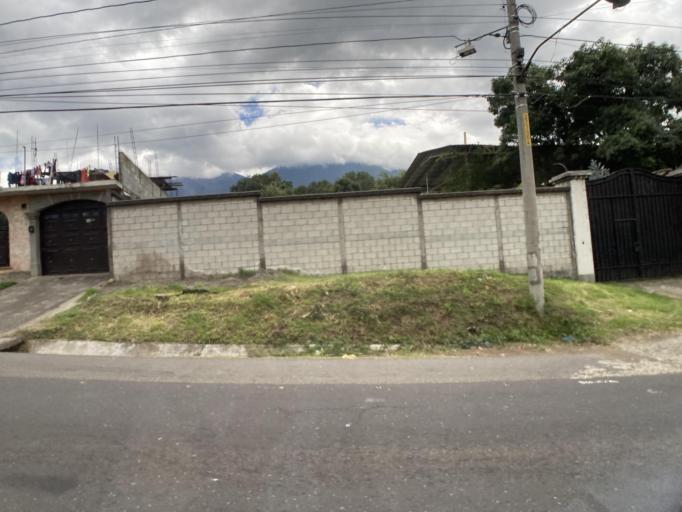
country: GT
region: Sacatepequez
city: Alotenango
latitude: 14.4817
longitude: -90.8085
